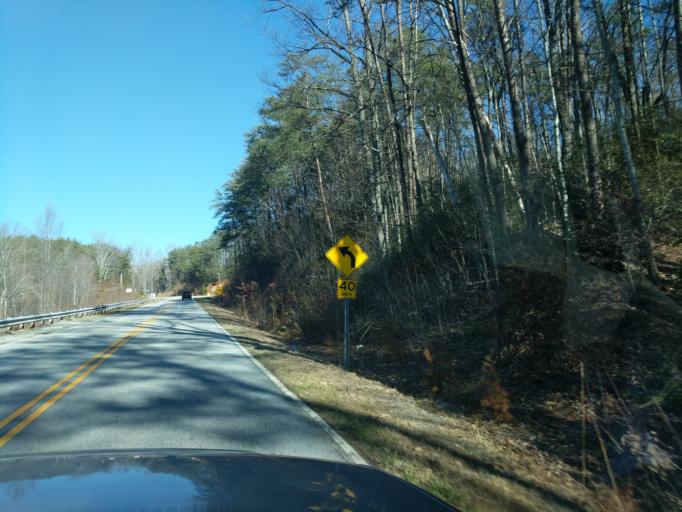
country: US
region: South Carolina
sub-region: Oconee County
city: Westminster
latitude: 34.7501
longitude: -83.2385
